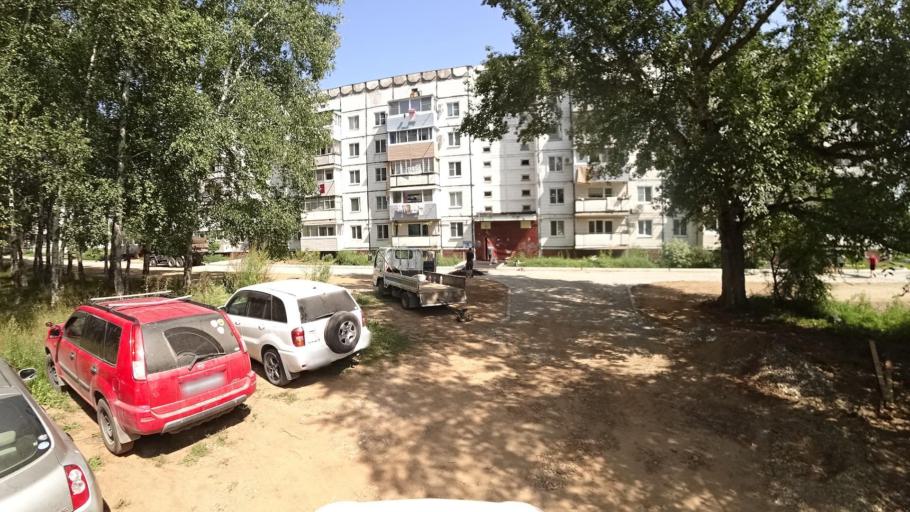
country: RU
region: Khabarovsk Krai
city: Khor
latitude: 47.9641
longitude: 135.1178
